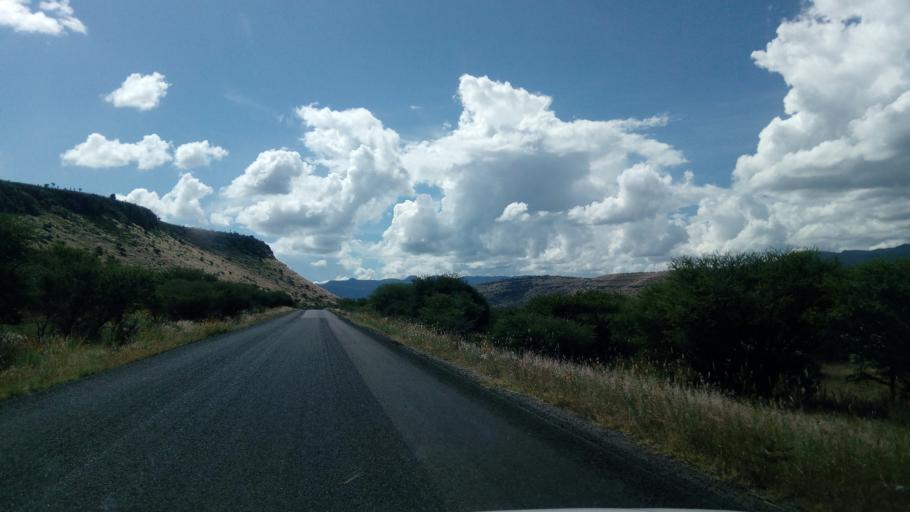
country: MX
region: Durango
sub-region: Durango
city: Jose Refugio Salcido
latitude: 23.8373
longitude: -104.4808
